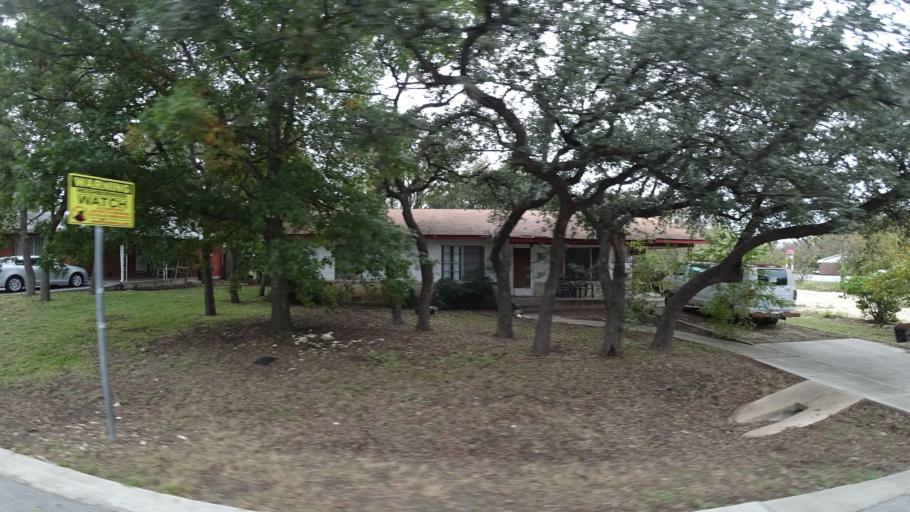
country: US
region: Texas
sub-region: Williamson County
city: Round Rock
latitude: 30.5113
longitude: -97.6933
